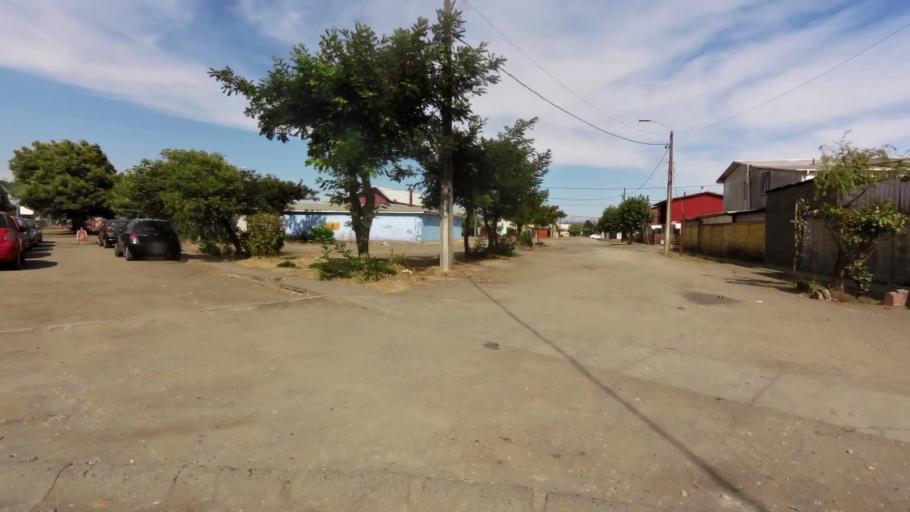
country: CL
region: Biobio
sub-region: Provincia de Concepcion
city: Talcahuano
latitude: -36.7884
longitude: -73.1077
